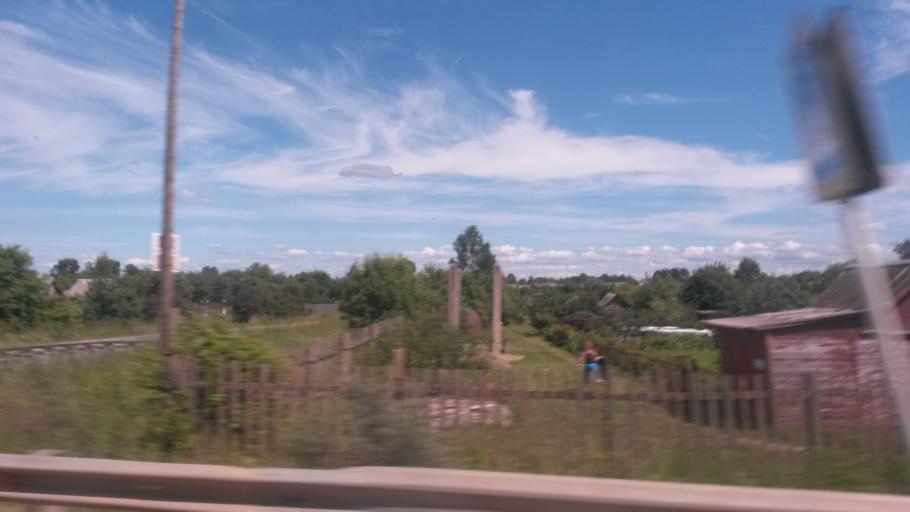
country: RU
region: Ivanovo
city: Staraya Vichuga
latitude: 57.2198
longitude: 41.8628
